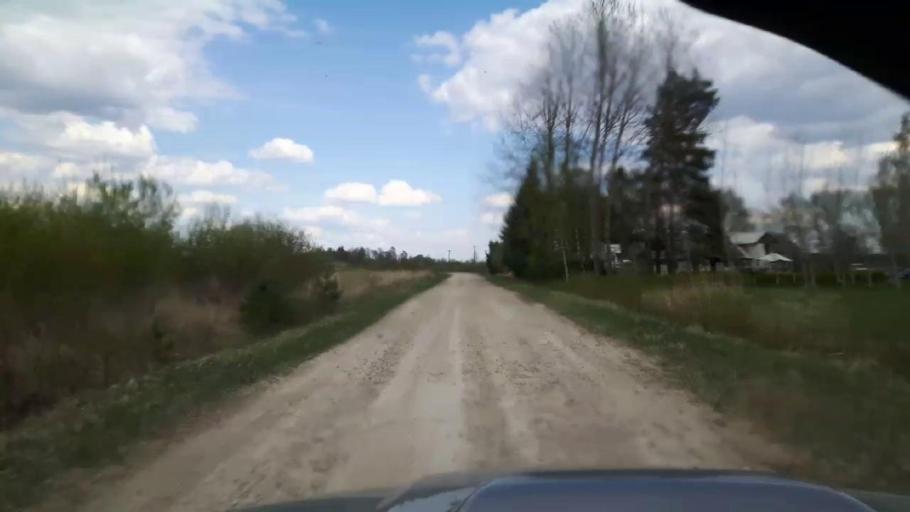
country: EE
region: Paernumaa
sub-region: Sindi linn
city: Sindi
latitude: 58.4098
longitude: 24.6949
